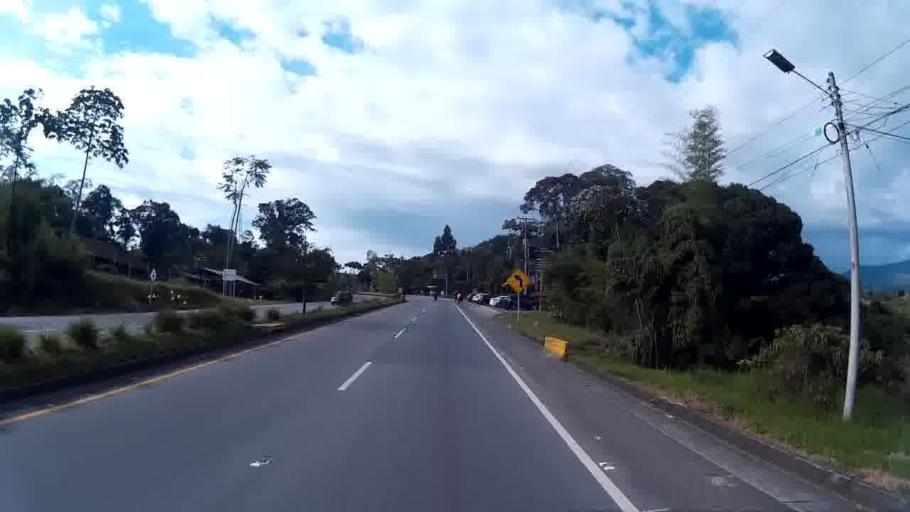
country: CO
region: Quindio
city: Circasia
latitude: 4.5912
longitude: -75.6411
